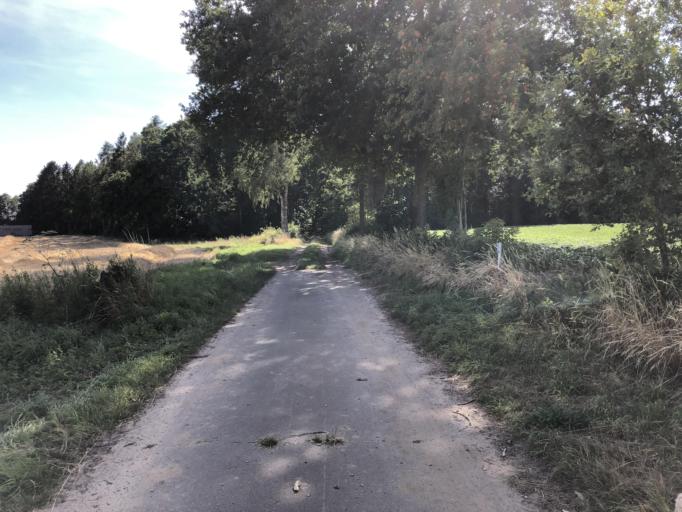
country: DE
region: Lower Saxony
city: Thomasburg
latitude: 53.1959
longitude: 10.6847
